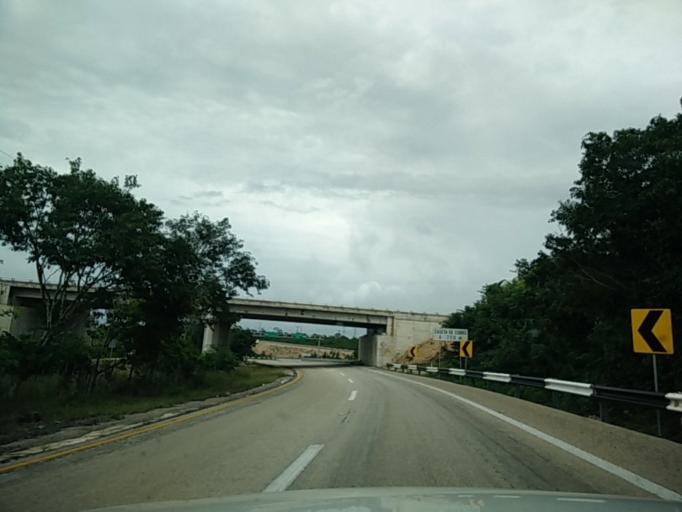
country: MX
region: Quintana Roo
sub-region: Lazaro Cardenas
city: El Tintal
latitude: 20.8979
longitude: -87.4418
